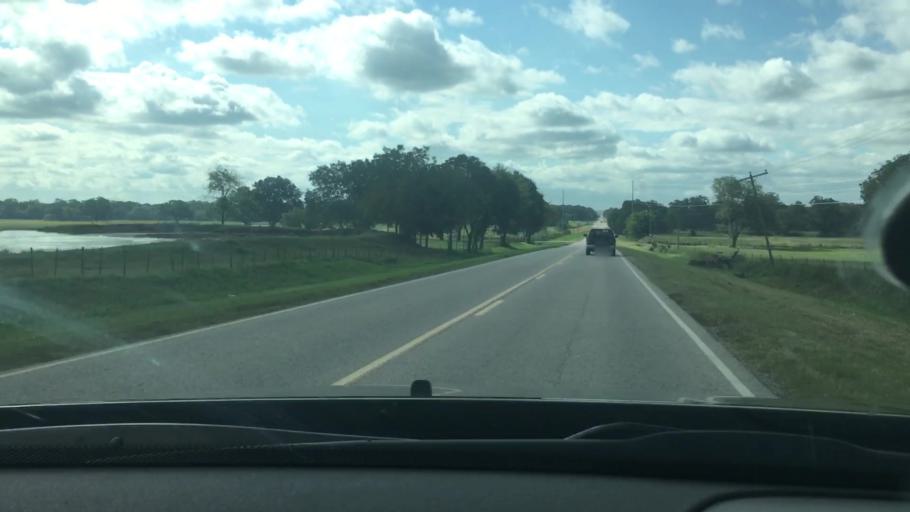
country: US
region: Oklahoma
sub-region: Pontotoc County
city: Ada
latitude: 34.7112
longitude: -96.6349
